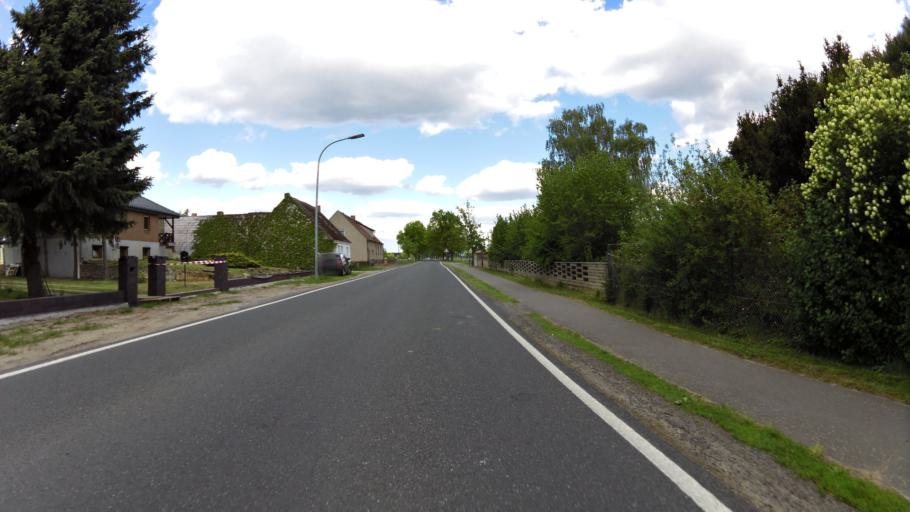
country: DE
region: Brandenburg
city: Schlepzig
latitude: 52.0842
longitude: 13.8935
